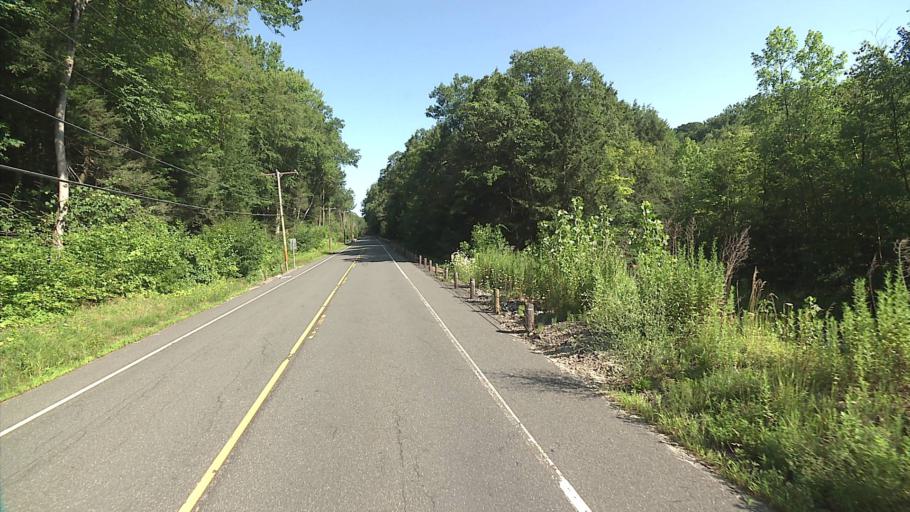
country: US
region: Connecticut
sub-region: Hartford County
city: North Granby
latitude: 41.9634
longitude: -72.8586
